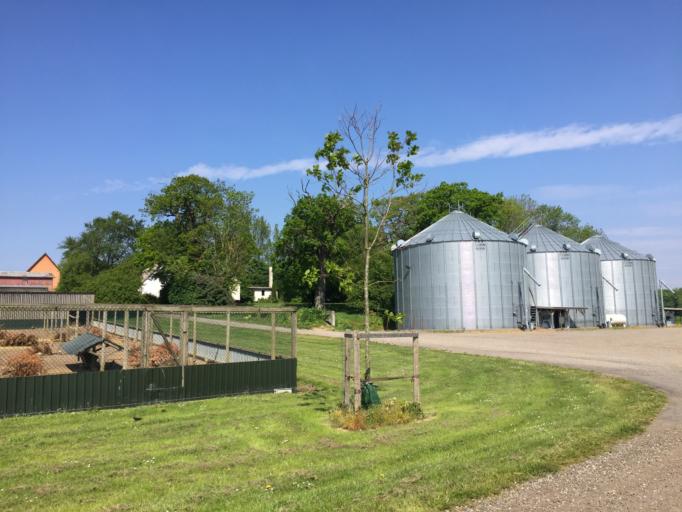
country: DK
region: South Denmark
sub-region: Langeland Kommune
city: Rudkobing
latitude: 55.0153
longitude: 10.8551
